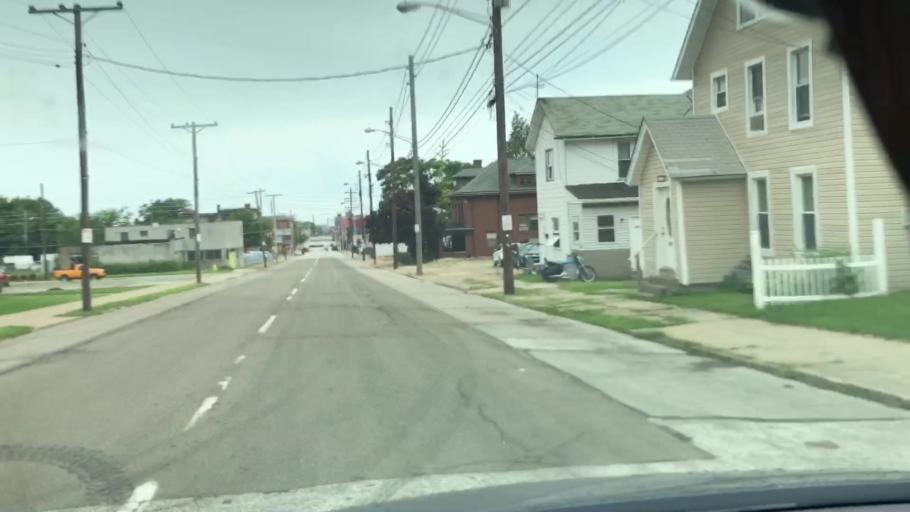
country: US
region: Pennsylvania
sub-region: Erie County
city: Erie
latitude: 42.1140
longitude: -80.0766
